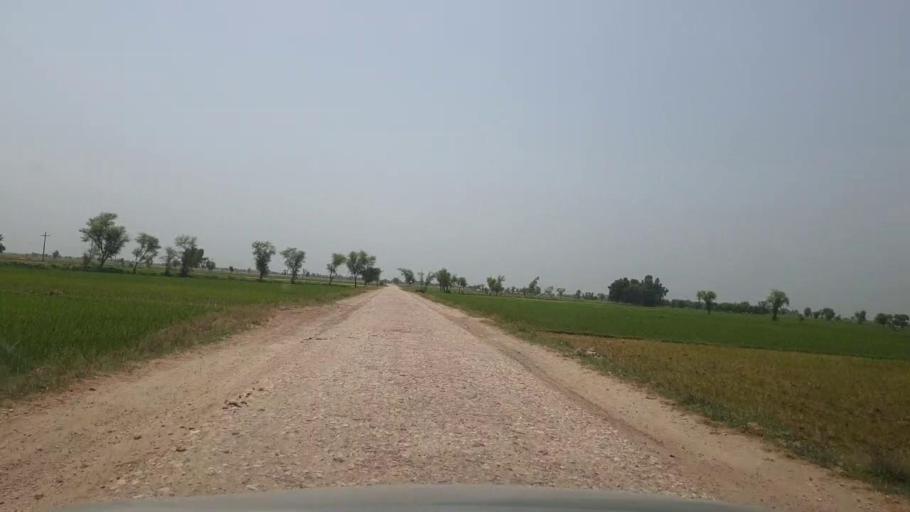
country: PK
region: Sindh
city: Garhi Yasin
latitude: 27.9224
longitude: 68.4040
